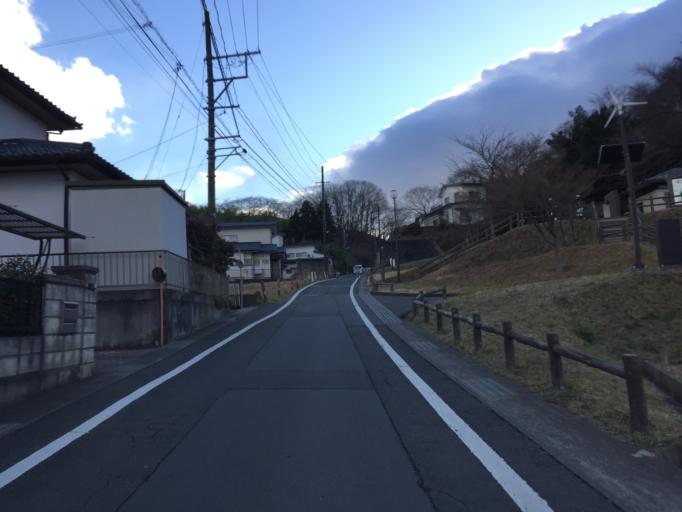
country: JP
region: Fukushima
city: Fukushima-shi
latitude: 37.7432
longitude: 140.4767
